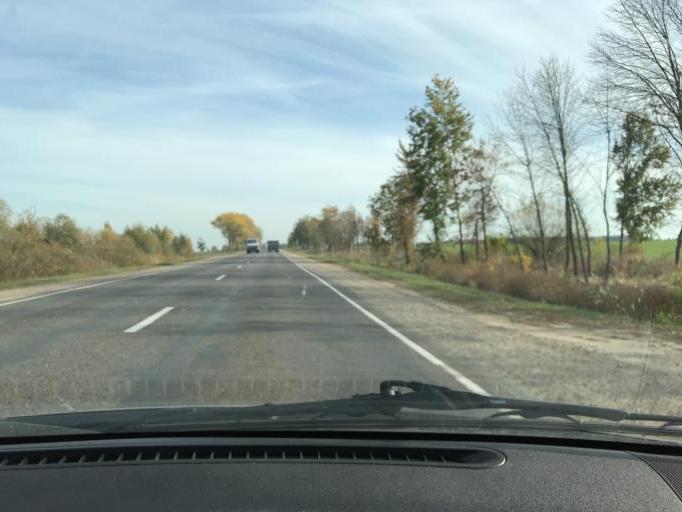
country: BY
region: Brest
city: Lahishyn
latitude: 52.2431
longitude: 25.9957
